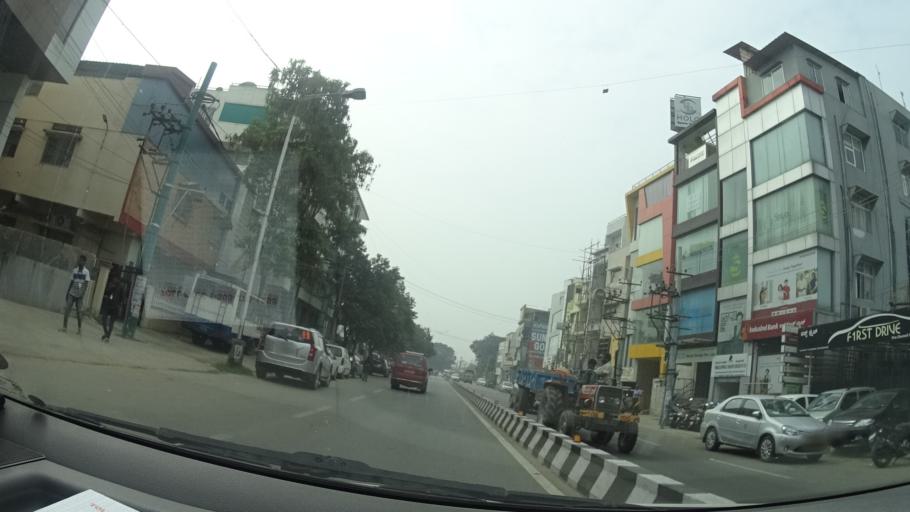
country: IN
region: Karnataka
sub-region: Bangalore Urban
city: Bangalore
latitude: 13.0230
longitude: 77.6294
